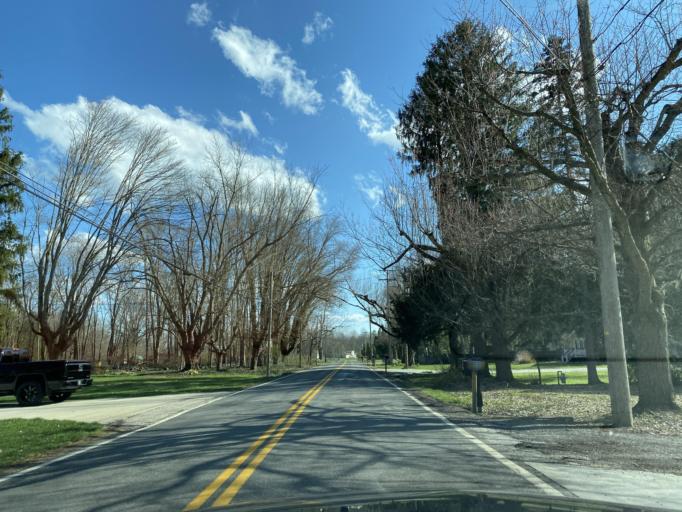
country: US
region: Ohio
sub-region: Summit County
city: Fairlawn
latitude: 41.0990
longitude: -81.6031
